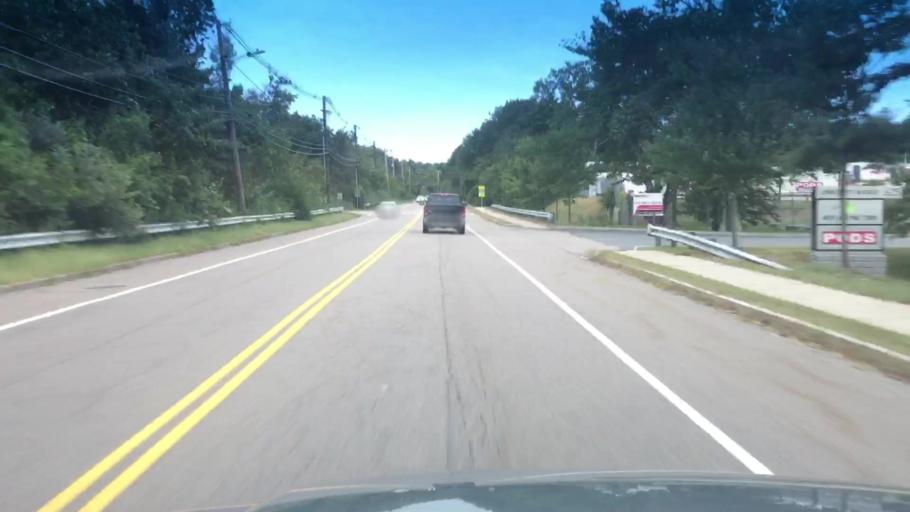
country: US
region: Massachusetts
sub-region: Norfolk County
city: Norwood
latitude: 42.2001
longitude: -71.1696
